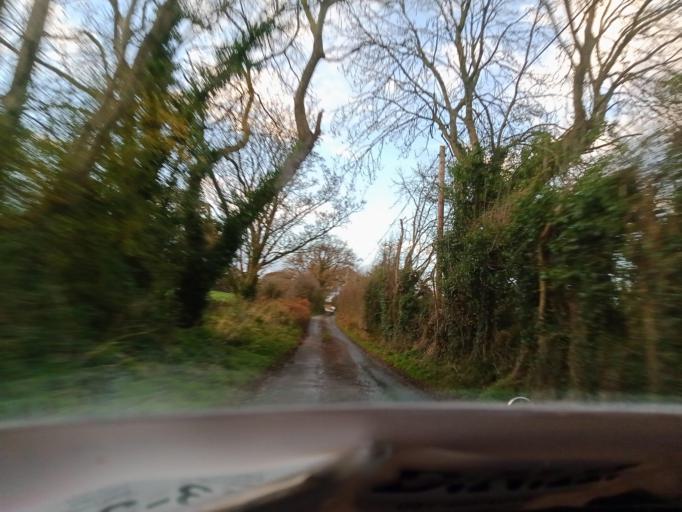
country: IE
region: Leinster
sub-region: Loch Garman
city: New Ross
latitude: 52.3366
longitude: -7.0092
